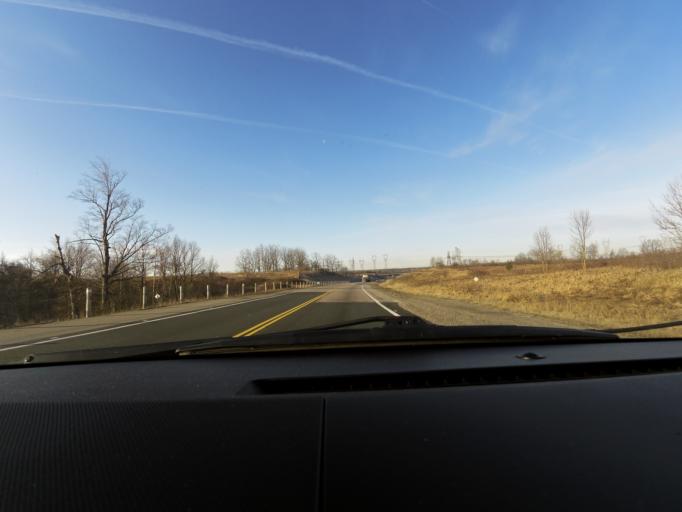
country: CA
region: Ontario
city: Ancaster
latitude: 43.0869
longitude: -79.9611
